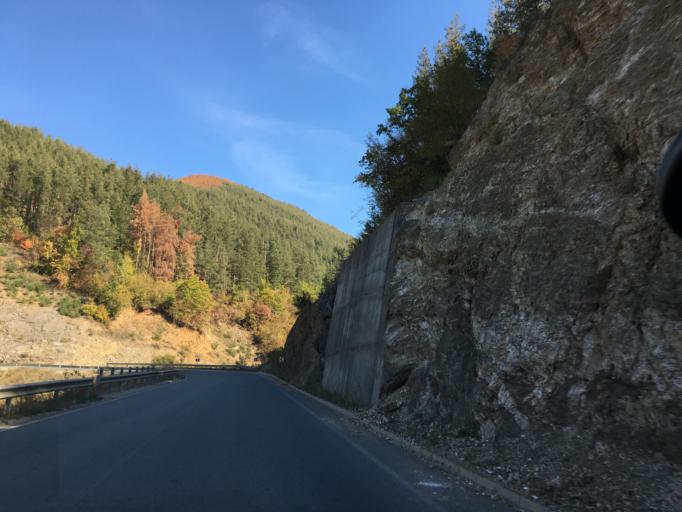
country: BG
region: Smolyan
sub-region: Obshtina Devin
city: Devin
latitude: 41.7447
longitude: 24.4325
